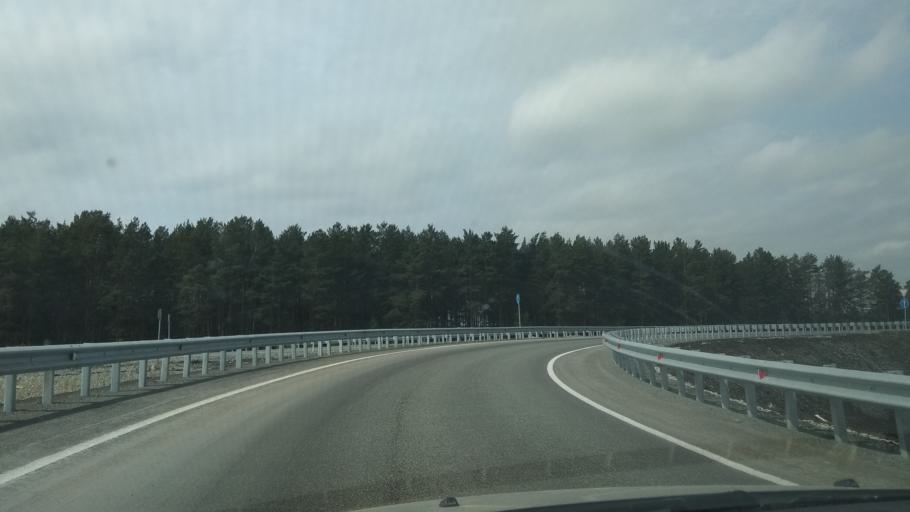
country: RU
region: Sverdlovsk
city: Istok
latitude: 56.8015
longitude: 60.7919
